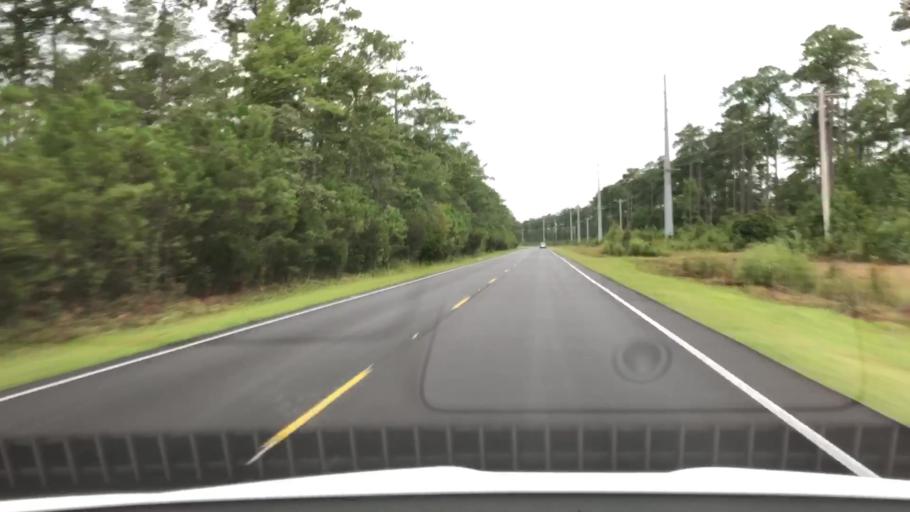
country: US
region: North Carolina
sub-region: Onslow County
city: Swansboro
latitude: 34.7831
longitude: -77.1131
